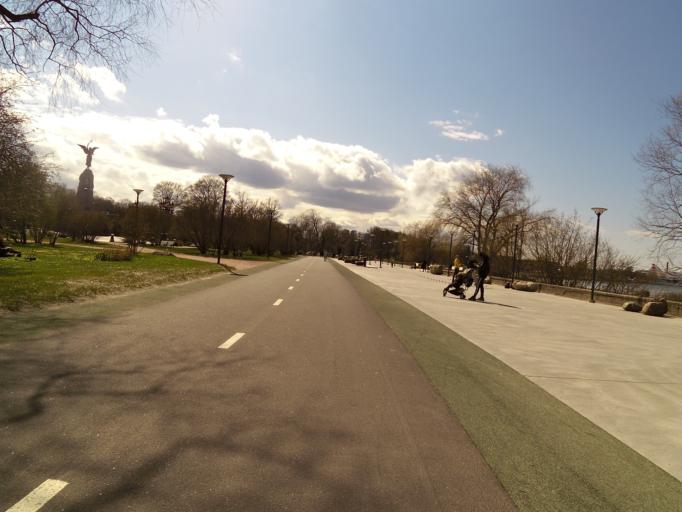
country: EE
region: Harju
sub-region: Tallinna linn
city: Tallinn
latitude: 59.4441
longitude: 24.7947
